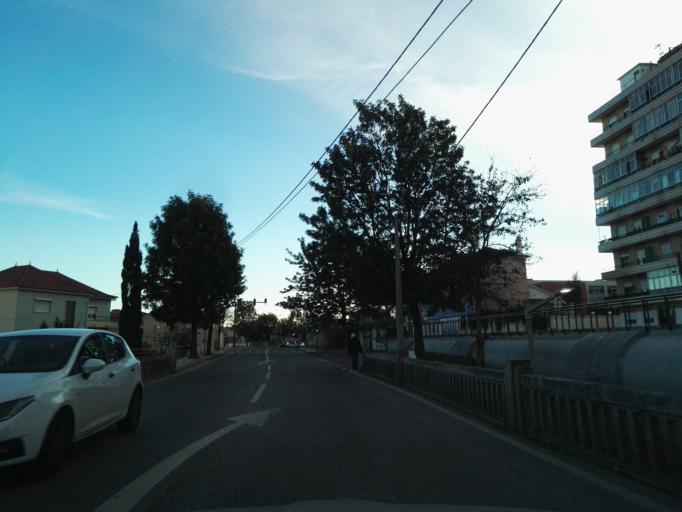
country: PT
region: Lisbon
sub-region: Vila Franca de Xira
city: Povoa de Santa Iria
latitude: 38.8615
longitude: -9.0651
